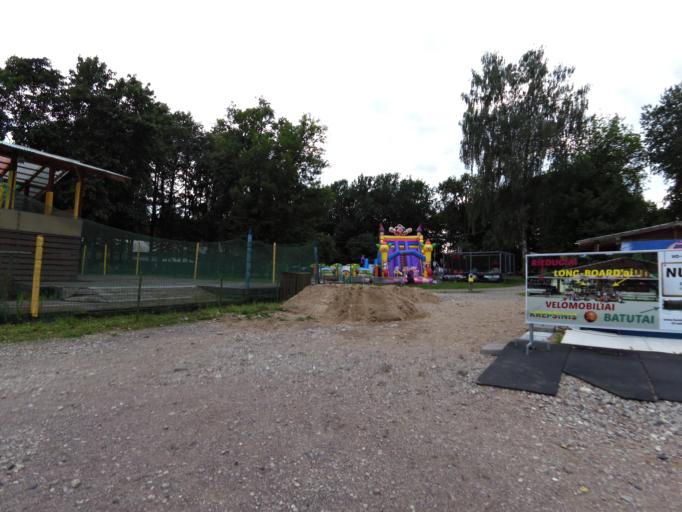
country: LT
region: Vilnius County
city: Vilkpede
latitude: 54.6832
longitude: 25.2350
